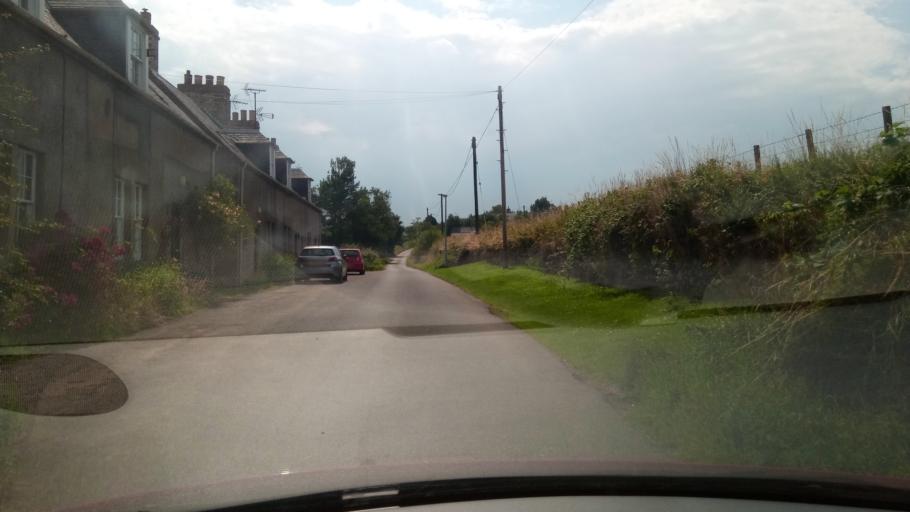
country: GB
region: Scotland
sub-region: The Scottish Borders
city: Kelso
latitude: 55.5708
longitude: -2.4739
